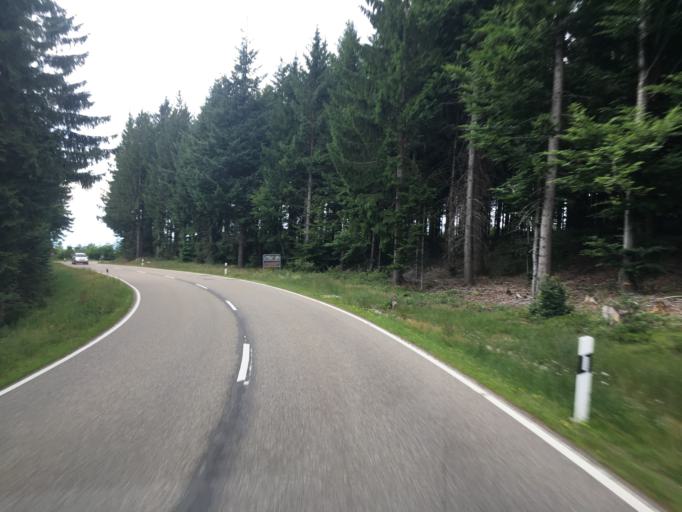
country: DE
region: Baden-Wuerttemberg
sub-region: Karlsruhe Region
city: Buhlertal
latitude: 48.6661
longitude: 8.2343
